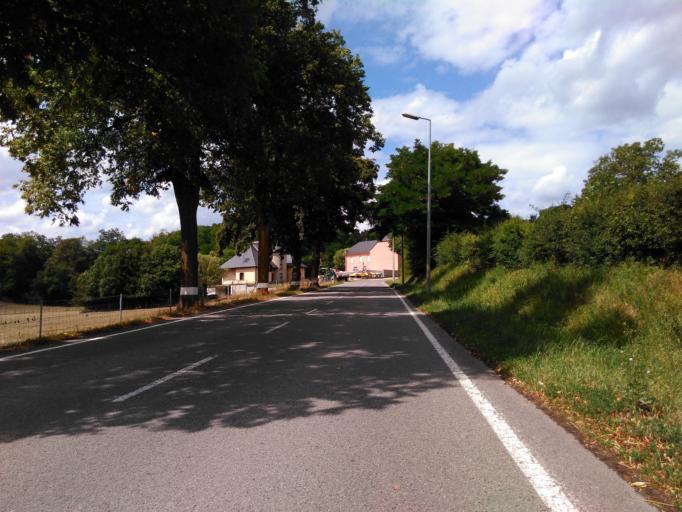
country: LU
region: Grevenmacher
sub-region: Canton de Grevenmacher
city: Junglinster
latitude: 49.7306
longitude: 6.3028
